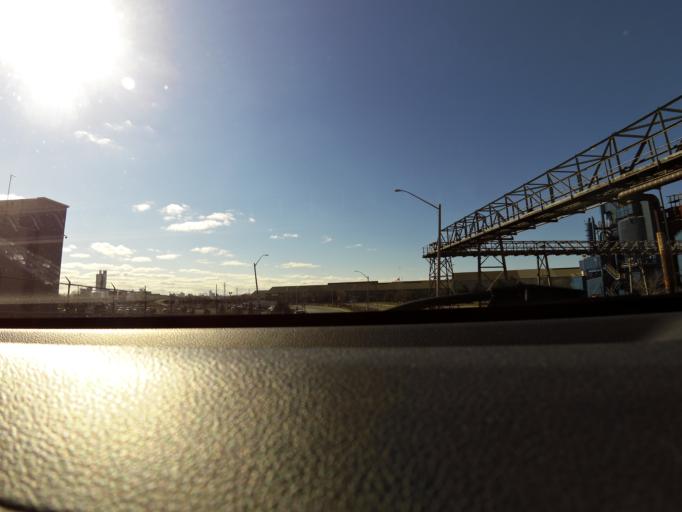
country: CA
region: Ontario
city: Hamilton
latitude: 43.2648
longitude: -79.8228
